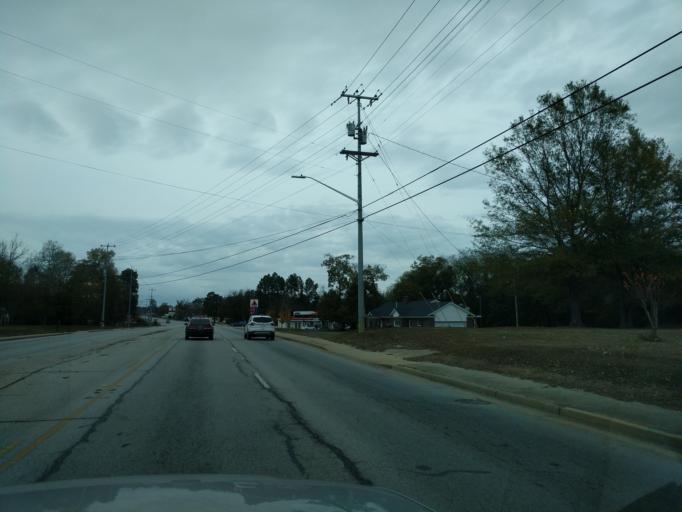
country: US
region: South Carolina
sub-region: Newberry County
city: Newberry
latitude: 34.2981
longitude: -81.6209
